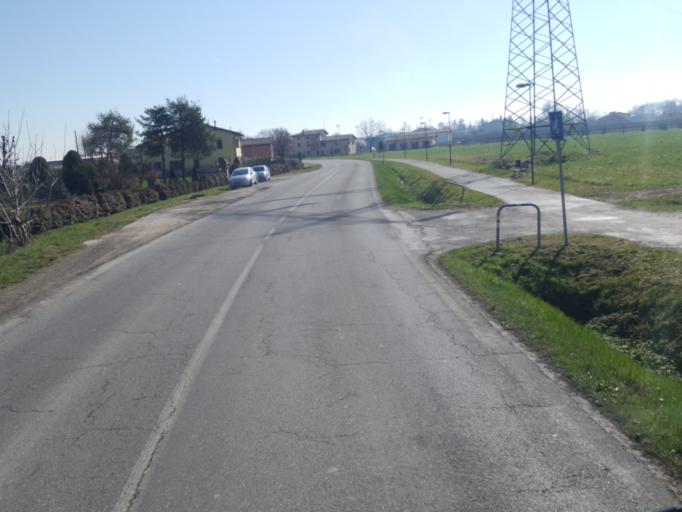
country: IT
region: Emilia-Romagna
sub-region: Provincia di Modena
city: Solara
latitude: 44.7727
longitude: 11.0829
